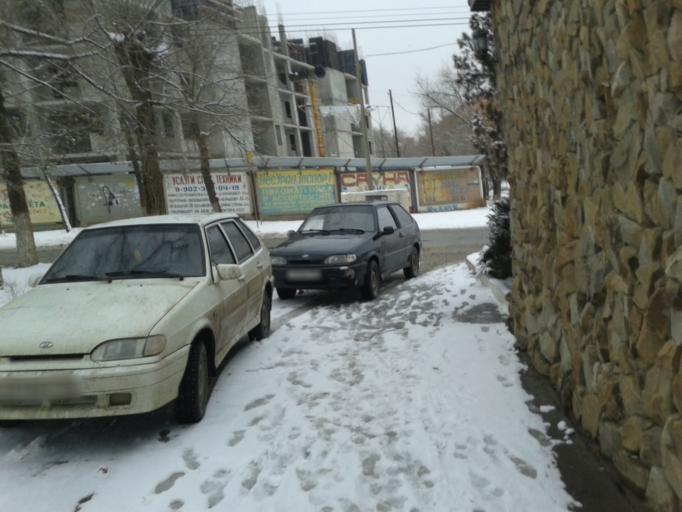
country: RU
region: Volgograd
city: Krasnoslobodsk
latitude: 48.5273
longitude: 44.5605
